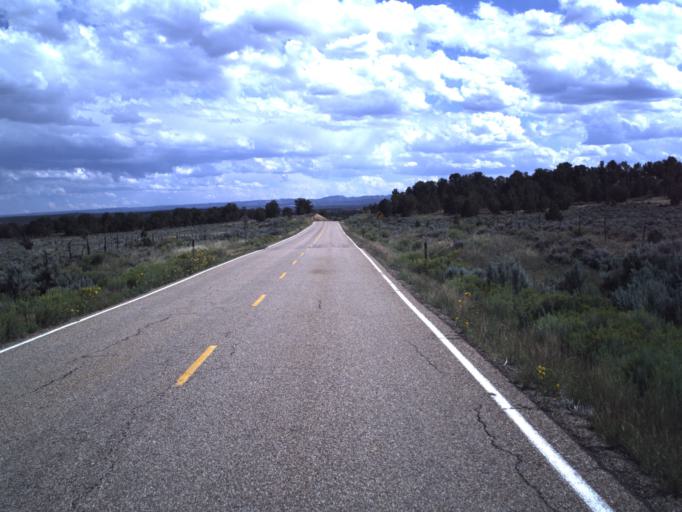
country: US
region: Utah
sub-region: Duchesne County
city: Duchesne
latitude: 40.2970
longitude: -110.6957
